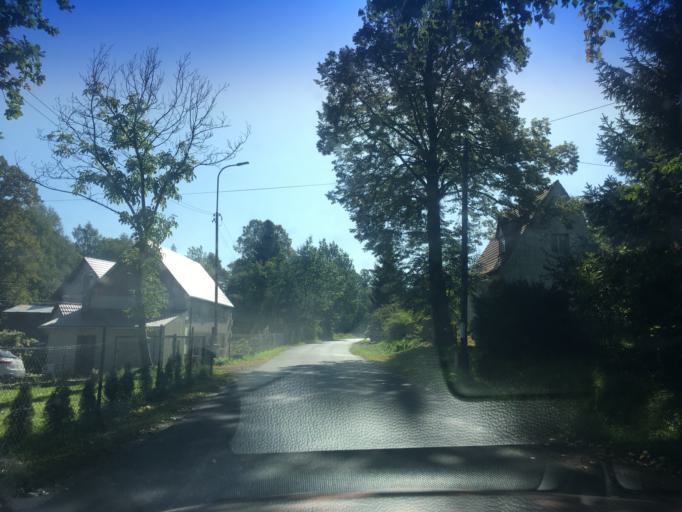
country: PL
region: Lower Silesian Voivodeship
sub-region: Powiat lubanski
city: Siekierczyn
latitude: 51.0592
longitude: 15.1719
